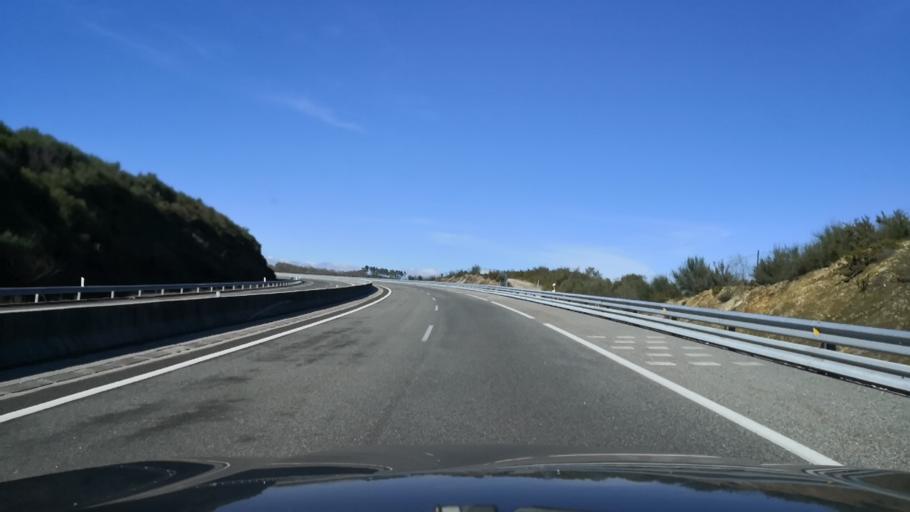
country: ES
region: Galicia
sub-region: Provincia de Pontevedra
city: Dozon
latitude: 42.5521
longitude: -8.0182
